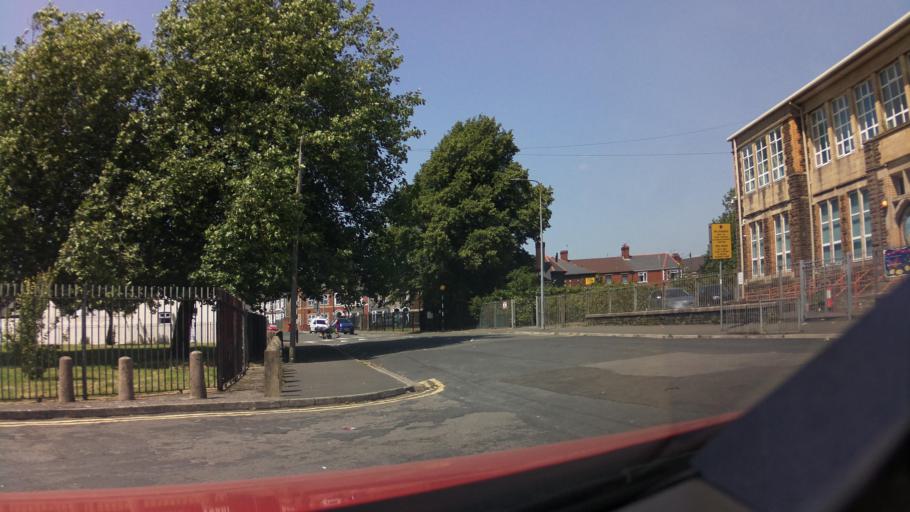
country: GB
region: Wales
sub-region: Cardiff
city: Cardiff
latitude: 51.4797
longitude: -3.1474
